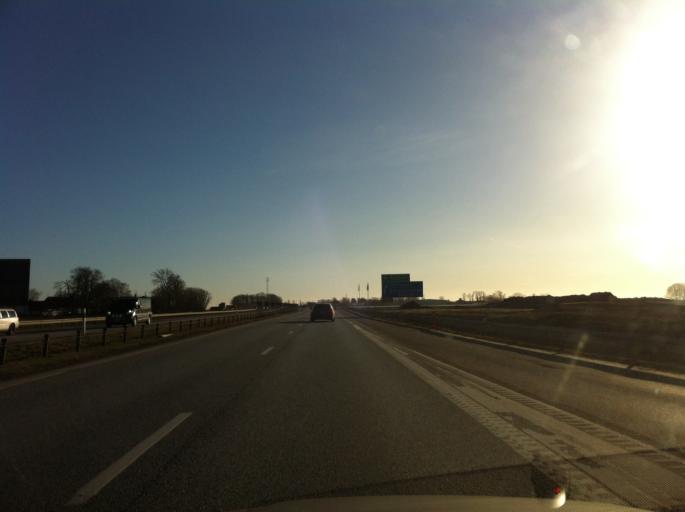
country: SE
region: Skane
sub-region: Angelholms Kommun
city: AEngelholm
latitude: 56.1910
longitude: 12.8553
